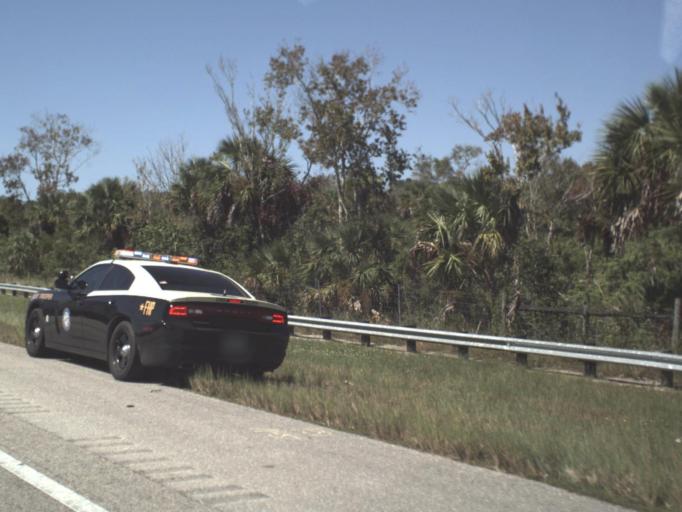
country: US
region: Florida
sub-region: Collier County
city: Orangetree
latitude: 26.1532
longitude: -81.5321
